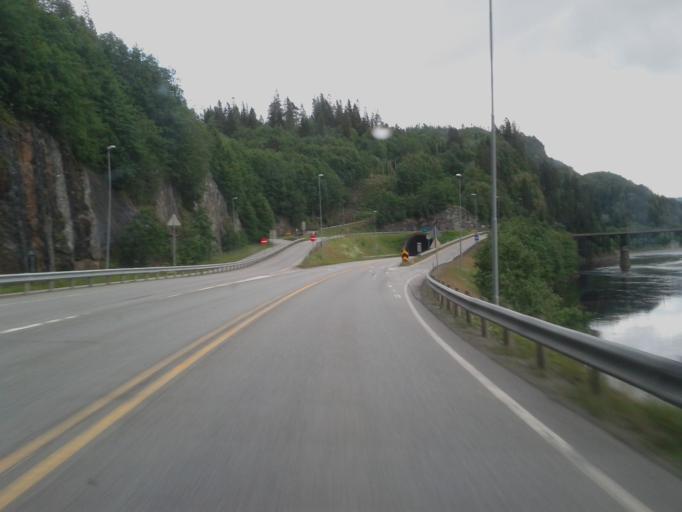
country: NO
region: Sor-Trondelag
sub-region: Midtre Gauldal
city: Storen
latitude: 63.0682
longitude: 10.2847
